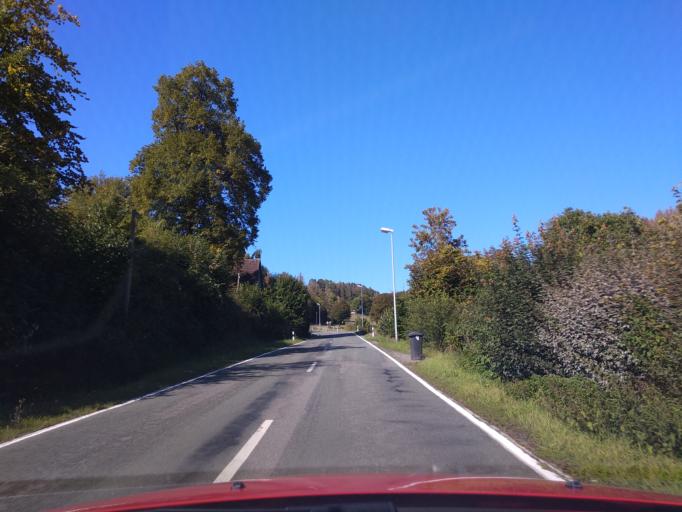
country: DE
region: North Rhine-Westphalia
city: Beverungen
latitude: 51.7158
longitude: 9.2885
